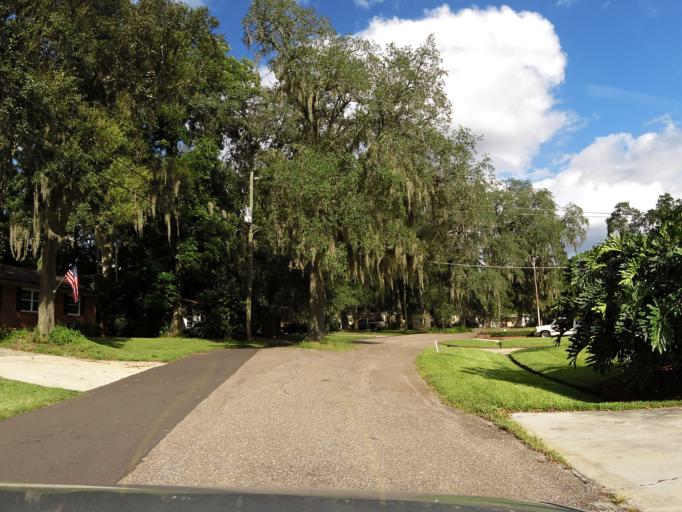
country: US
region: Florida
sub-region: Duval County
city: Jacksonville
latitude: 30.2904
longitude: -81.7407
